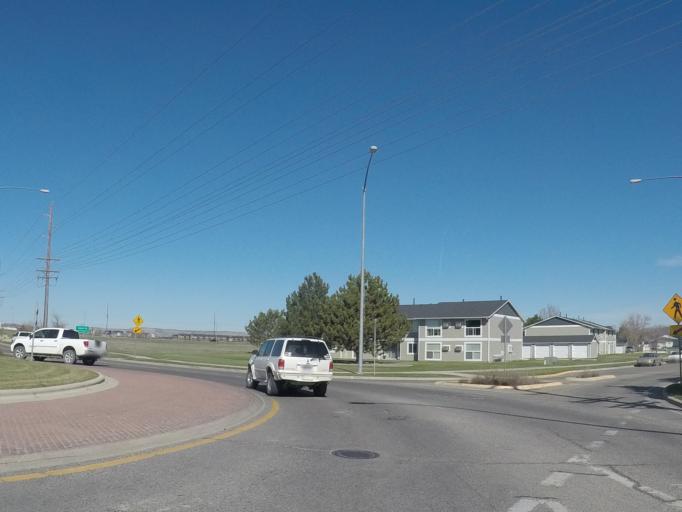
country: US
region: Montana
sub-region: Yellowstone County
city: Billings
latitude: 45.7551
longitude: -108.6133
